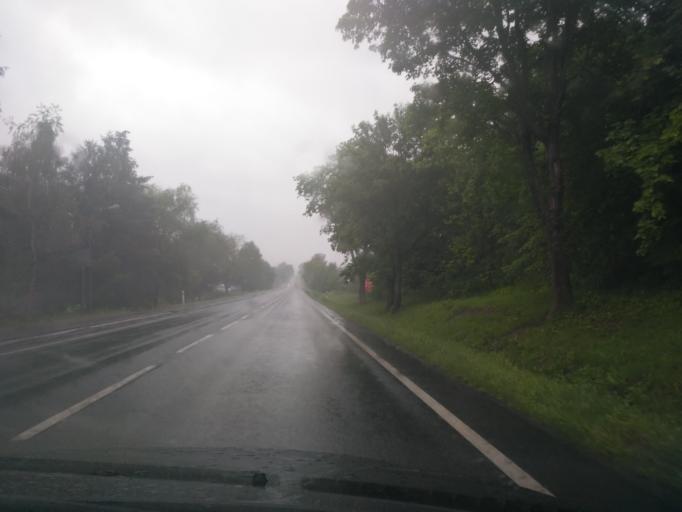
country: PL
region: Subcarpathian Voivodeship
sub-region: Powiat jasielski
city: Tarnowiec
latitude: 49.7631
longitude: 21.5669
